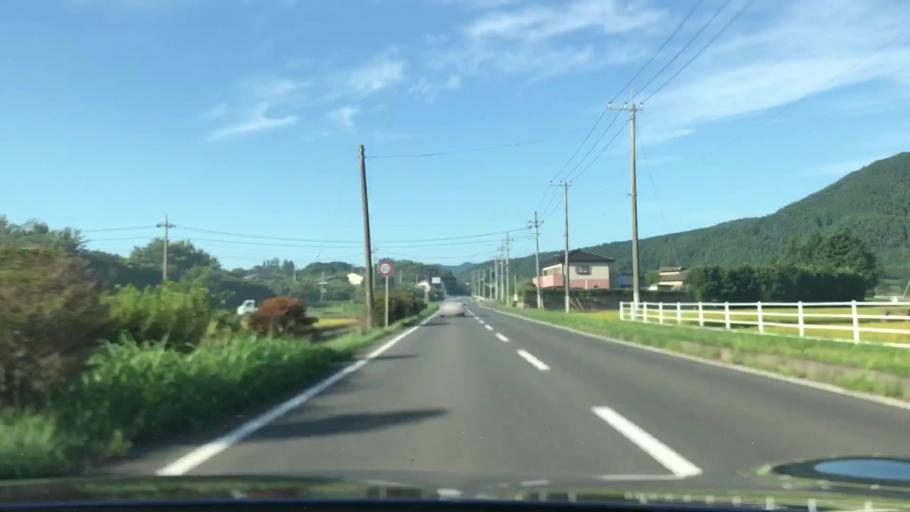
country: JP
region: Ibaraki
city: Makabe
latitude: 36.2562
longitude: 140.1705
